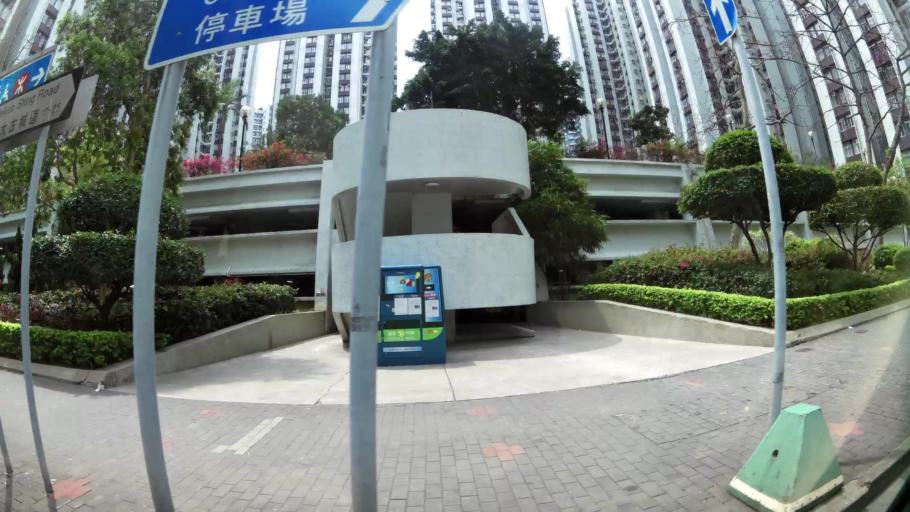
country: HK
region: Wanchai
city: Wan Chai
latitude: 22.2862
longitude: 114.2200
